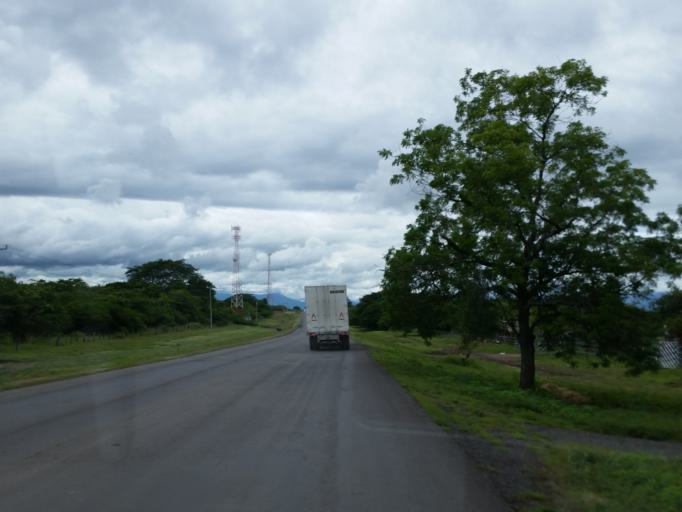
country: NI
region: Chinandega
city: Somotillo
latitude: 12.9142
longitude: -86.8514
